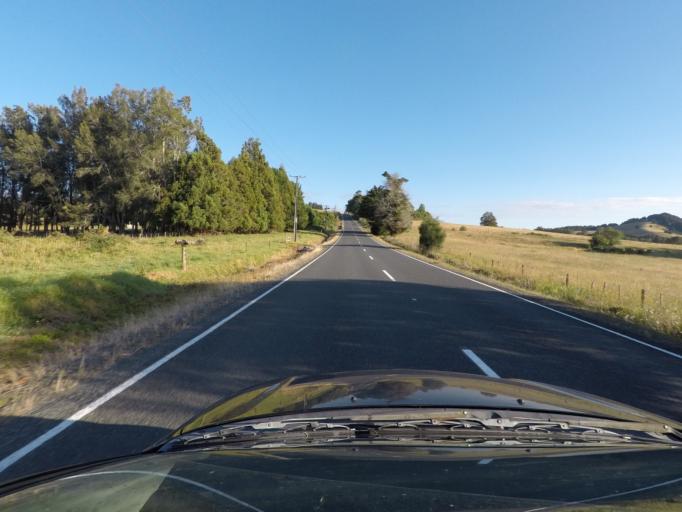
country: NZ
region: Northland
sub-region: Whangarei
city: Whangarei
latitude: -35.6745
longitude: 174.3266
